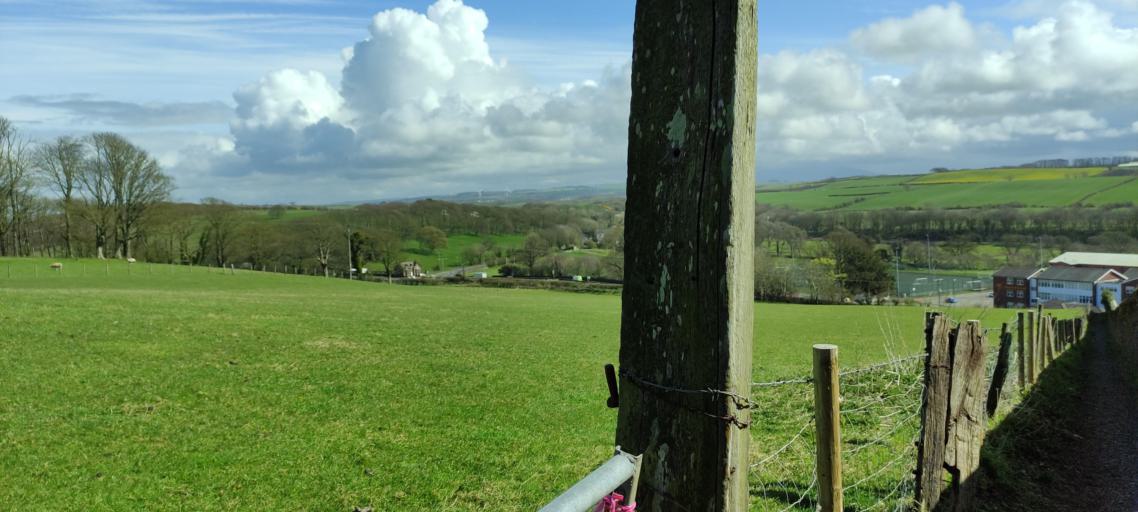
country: GB
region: England
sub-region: Cumbria
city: Maryport
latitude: 54.7199
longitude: -3.4881
